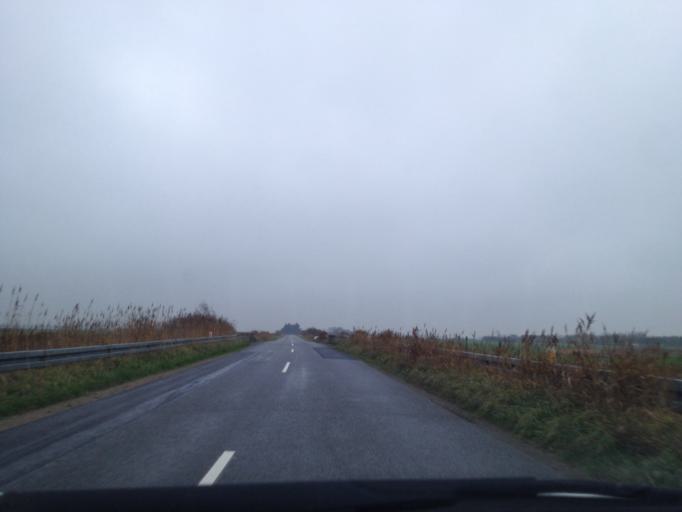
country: DK
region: South Denmark
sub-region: Tonder Kommune
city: Sherrebek
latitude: 55.1133
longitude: 8.7323
